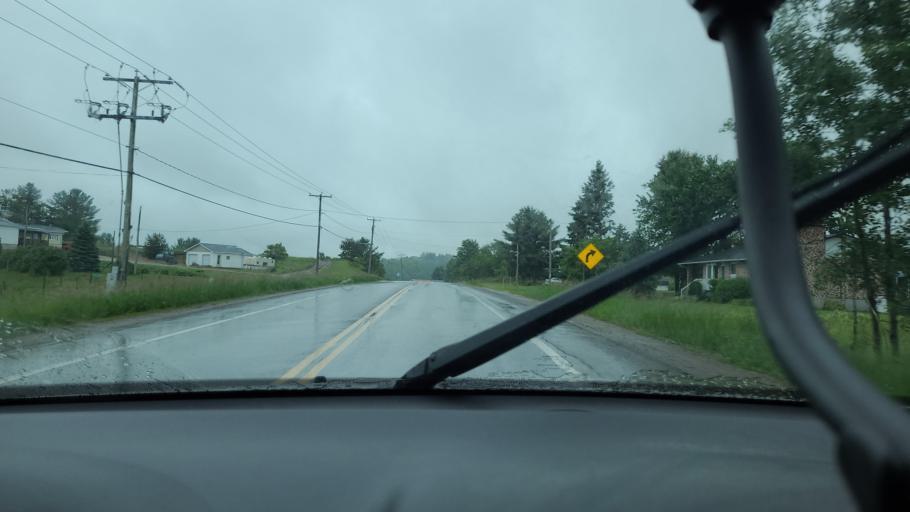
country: CA
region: Quebec
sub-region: Outaouais
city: Saint-Andre-Avellin
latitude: 45.7852
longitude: -75.0674
